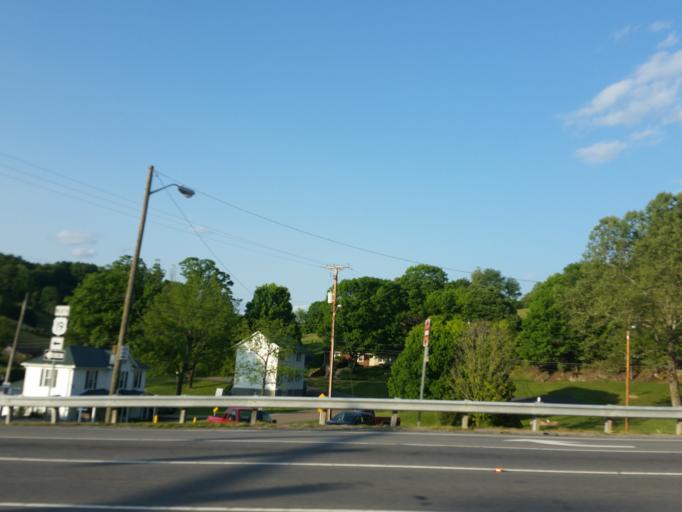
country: US
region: Virginia
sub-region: Washington County
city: Abingdon
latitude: 36.7462
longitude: -82.0521
